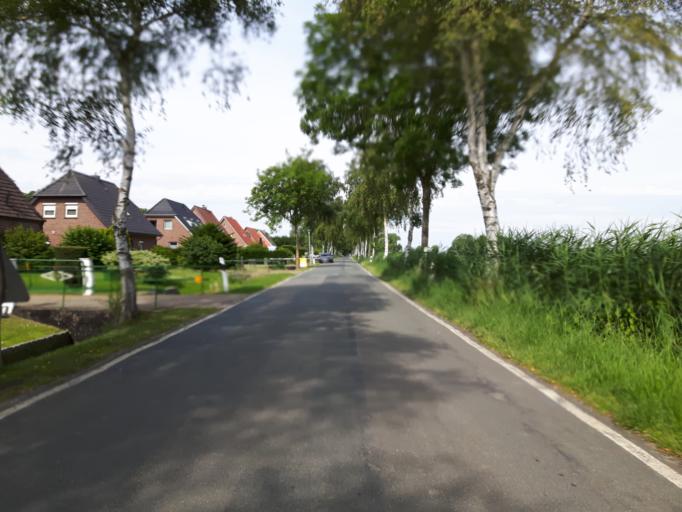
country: DE
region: Lower Saxony
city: Elsfleth
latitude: 53.2580
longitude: 8.4466
